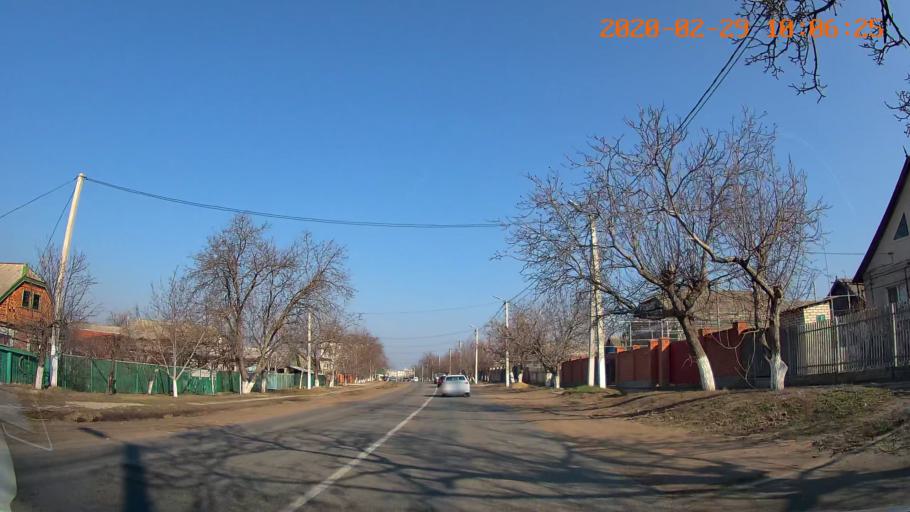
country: MD
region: Telenesti
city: Tiraspolul Nou
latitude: 46.8145
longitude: 29.6691
